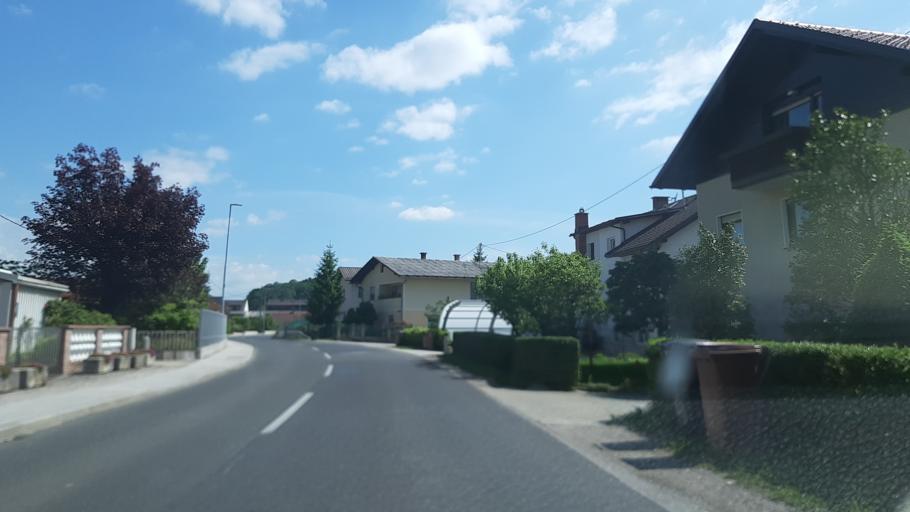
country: SI
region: Brezovica
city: Notranje Gorice
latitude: 45.9974
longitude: 14.4080
